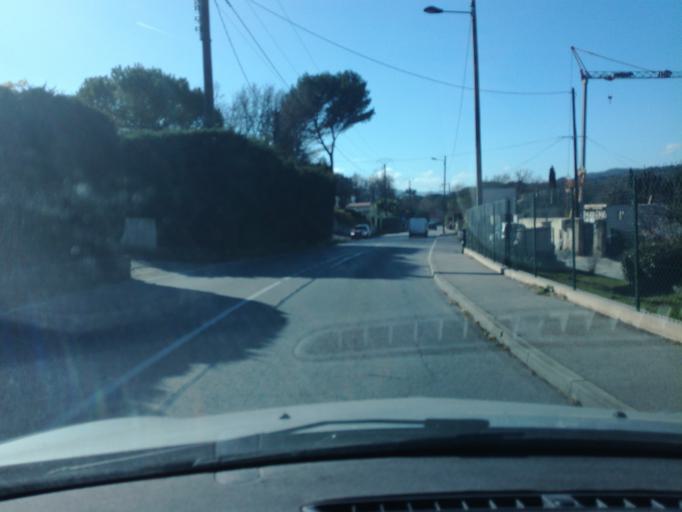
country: FR
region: Provence-Alpes-Cote d'Azur
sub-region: Departement des Alpes-Maritimes
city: Grasse
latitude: 43.6348
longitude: 6.9327
